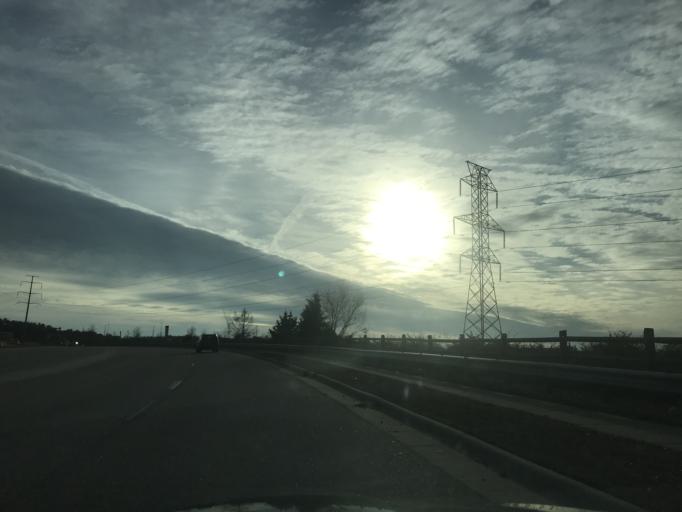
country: US
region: North Carolina
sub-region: Wake County
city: Raleigh
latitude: 35.8694
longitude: -78.5712
